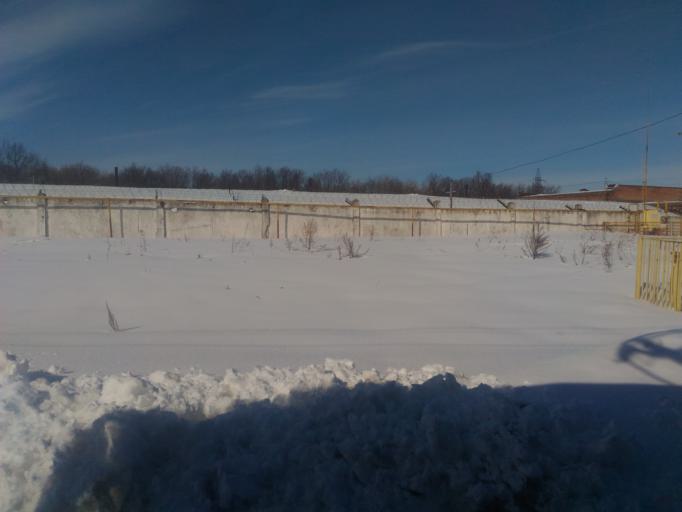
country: RU
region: Ulyanovsk
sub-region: Ulyanovskiy Rayon
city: Ulyanovsk
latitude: 54.3499
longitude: 48.3485
